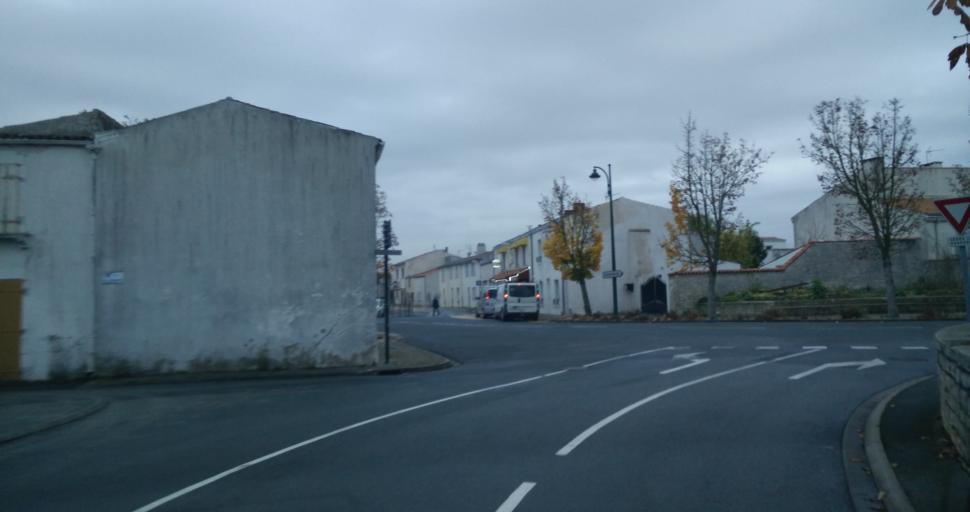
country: FR
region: Poitou-Charentes
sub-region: Departement de la Charente-Maritime
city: Puilboreau
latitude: 46.1879
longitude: -1.1185
